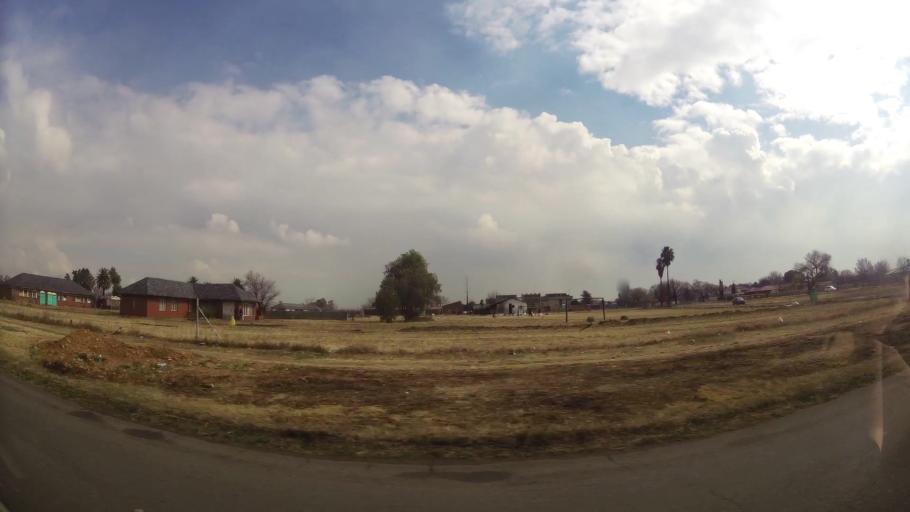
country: ZA
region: Gauteng
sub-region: Sedibeng District Municipality
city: Vereeniging
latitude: -26.6679
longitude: 27.9199
